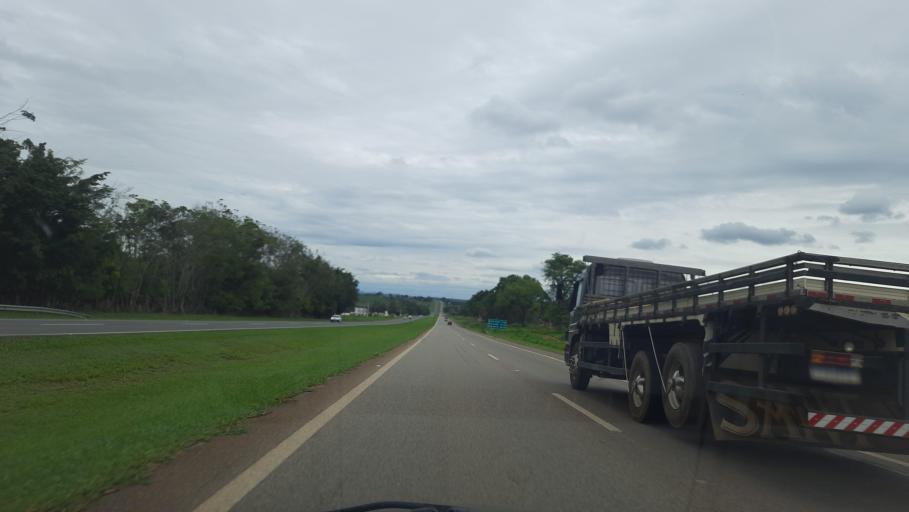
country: BR
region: Sao Paulo
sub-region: Moji-Guacu
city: Mogi-Gaucu
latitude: -22.2272
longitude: -46.9789
